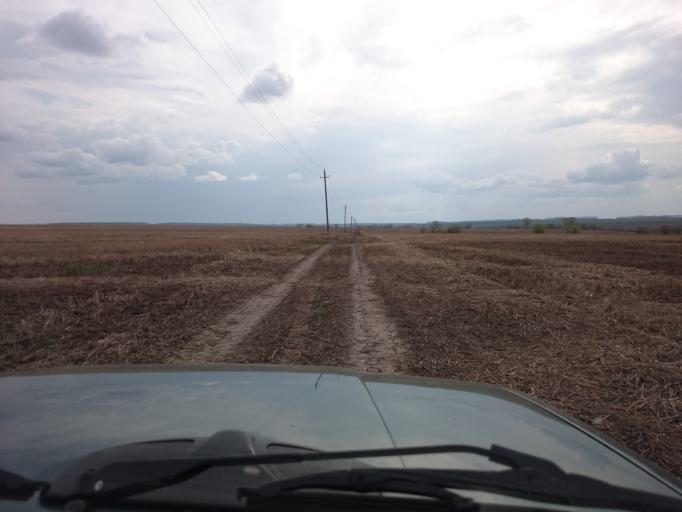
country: RU
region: Mordoviya
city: Kadoshkino
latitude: 54.0222
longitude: 44.4722
